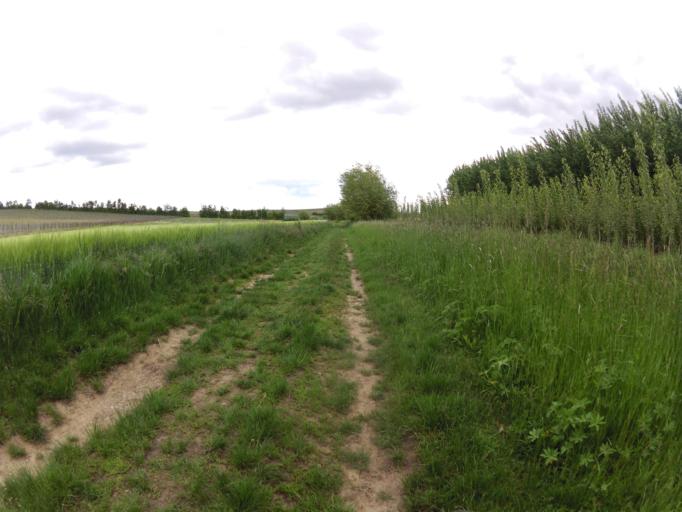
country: DE
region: Bavaria
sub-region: Regierungsbezirk Unterfranken
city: Volkach
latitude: 49.8876
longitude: 10.2339
